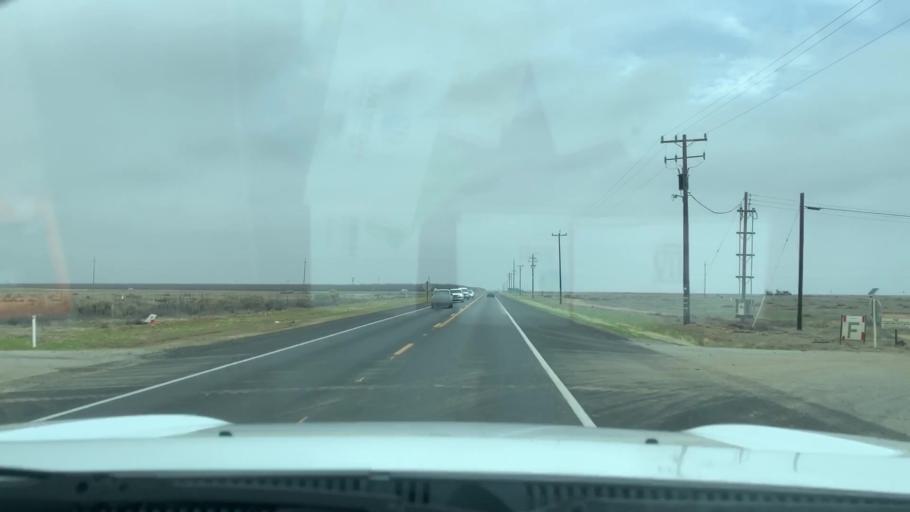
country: US
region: California
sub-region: Kern County
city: Lost Hills
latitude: 35.6158
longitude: -119.7389
